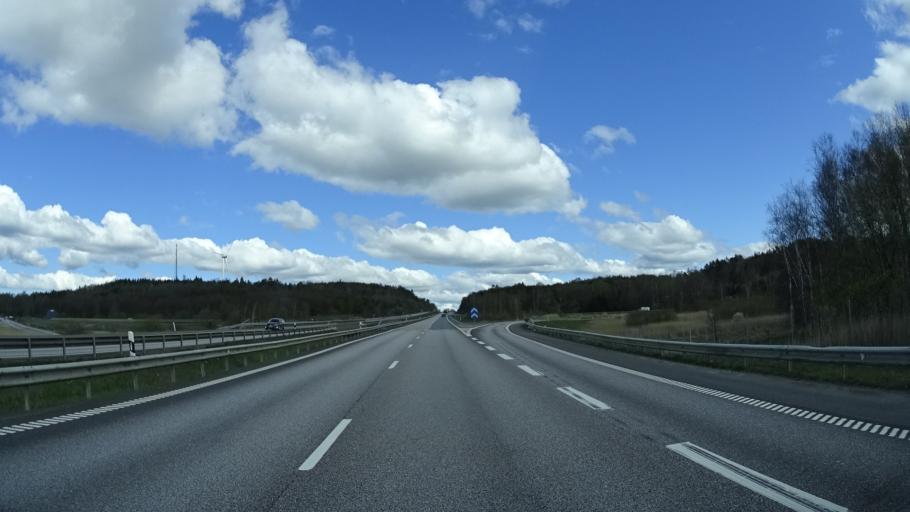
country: SE
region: Halland
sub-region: Kungsbacka Kommun
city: Frillesas
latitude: 57.3264
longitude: 12.2070
